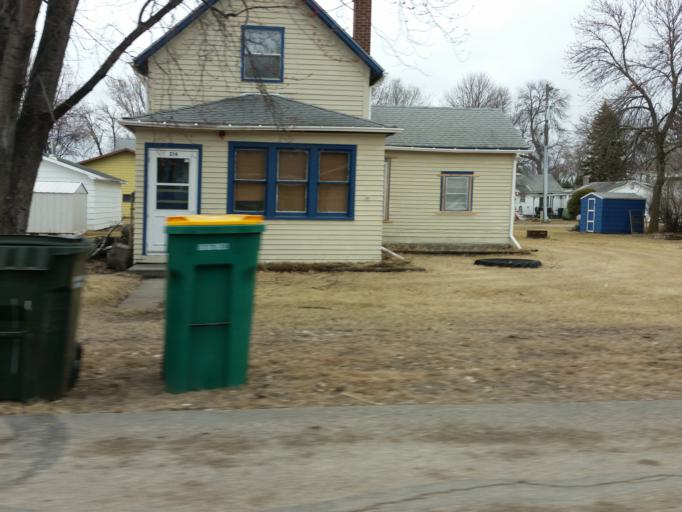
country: US
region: North Dakota
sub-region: Traill County
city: Hillsboro
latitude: 47.1904
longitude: -97.2161
